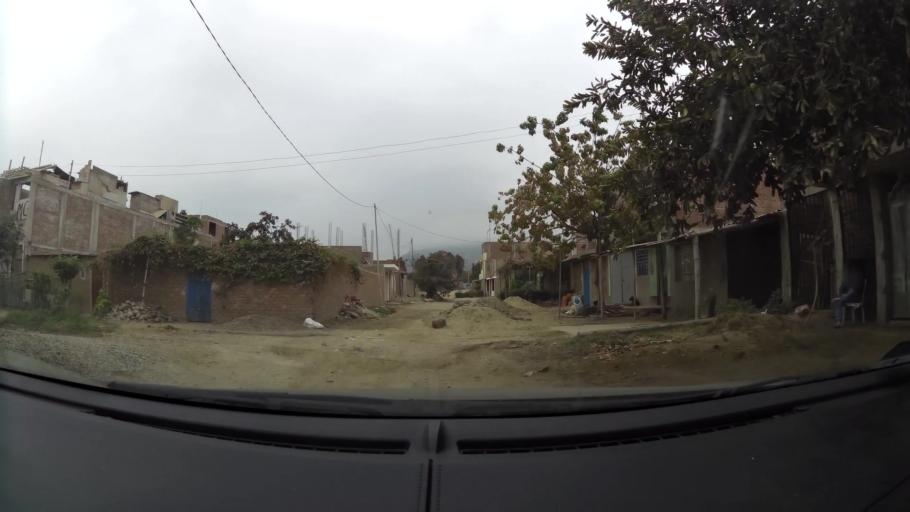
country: PE
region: La Libertad
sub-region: Provincia de Trujillo
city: La Esperanza
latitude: -8.0843
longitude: -79.0496
